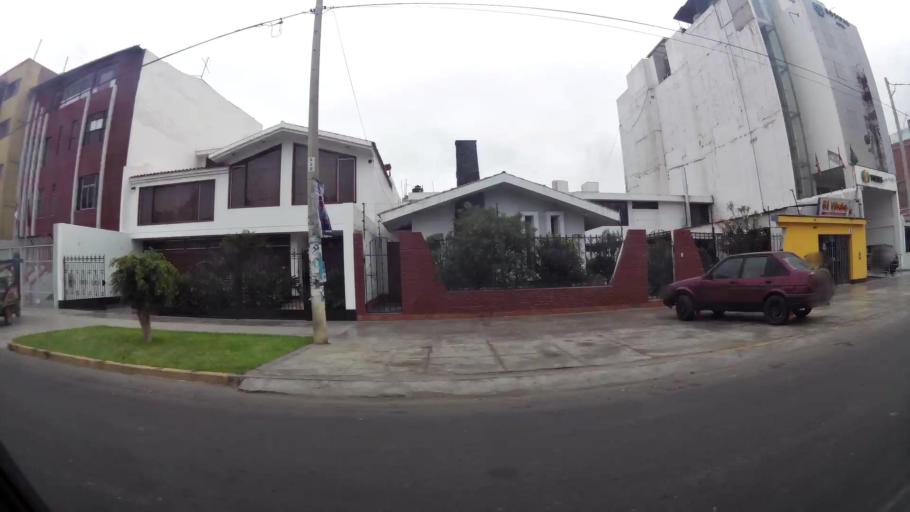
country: PE
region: La Libertad
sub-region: Provincia de Trujillo
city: Trujillo
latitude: -8.1227
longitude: -79.0373
